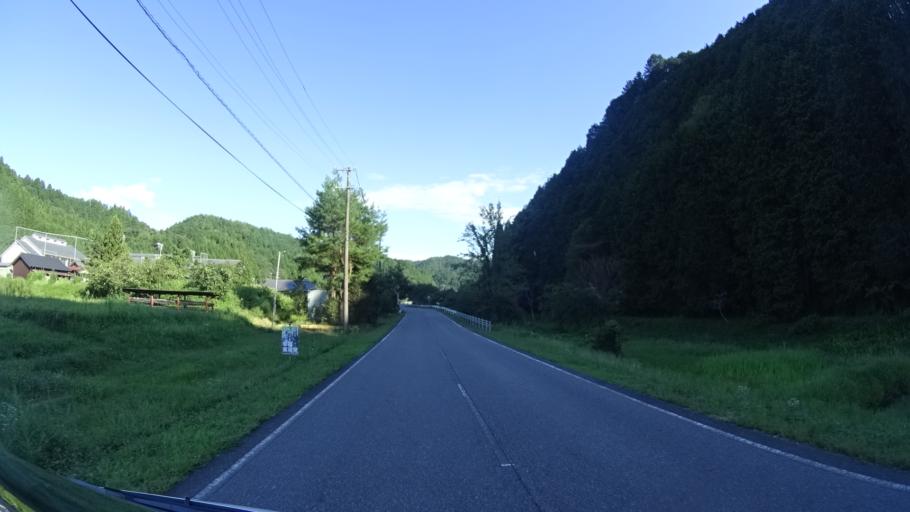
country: JP
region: Gifu
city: Minokamo
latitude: 35.5818
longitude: 137.0855
